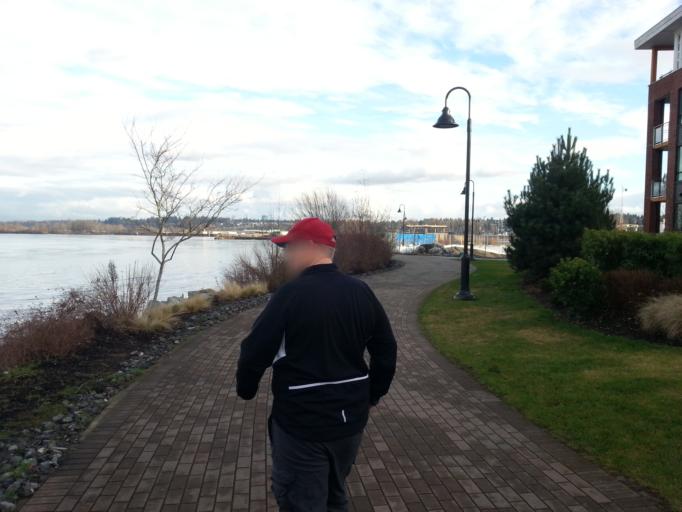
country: CA
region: British Columbia
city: New Westminster
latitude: 49.1960
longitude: -122.9225
